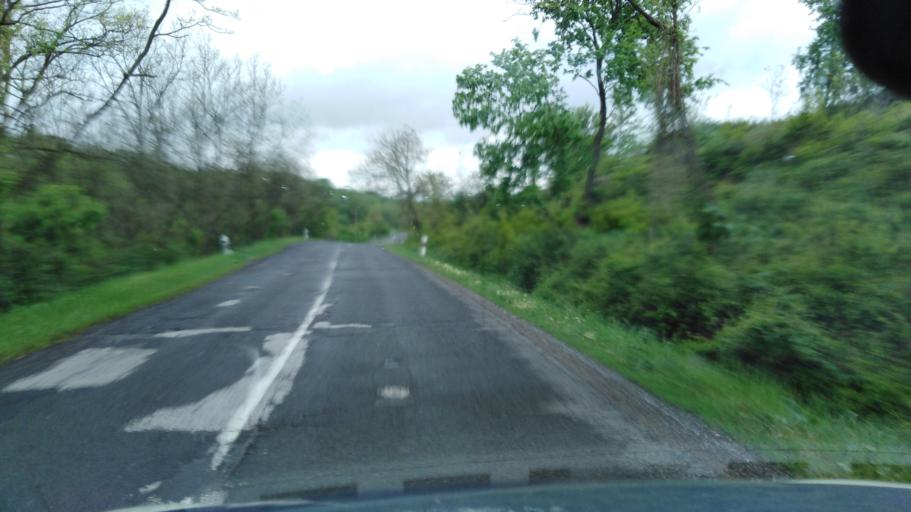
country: HU
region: Nograd
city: Rimoc
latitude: 48.0241
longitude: 19.5882
